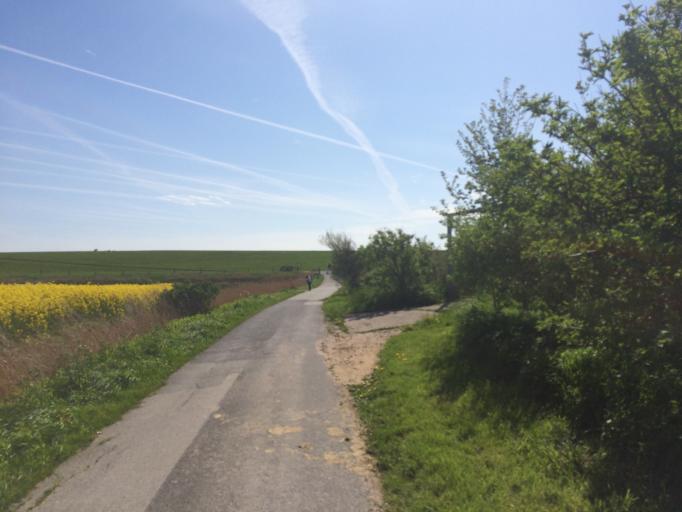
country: DE
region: Schleswig-Holstein
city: Dagebull
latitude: 54.7257
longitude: 8.7059
